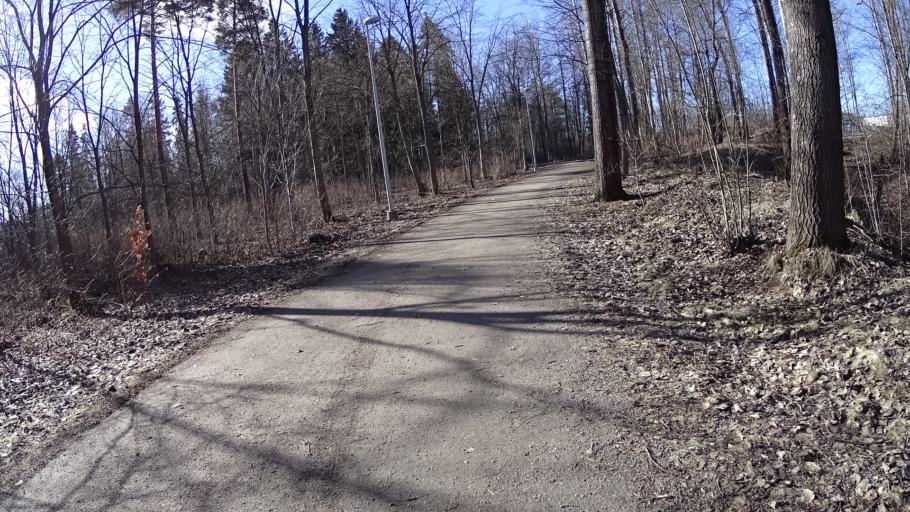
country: FI
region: Uusimaa
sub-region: Helsinki
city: Teekkarikylae
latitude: 60.2710
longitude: 24.8827
